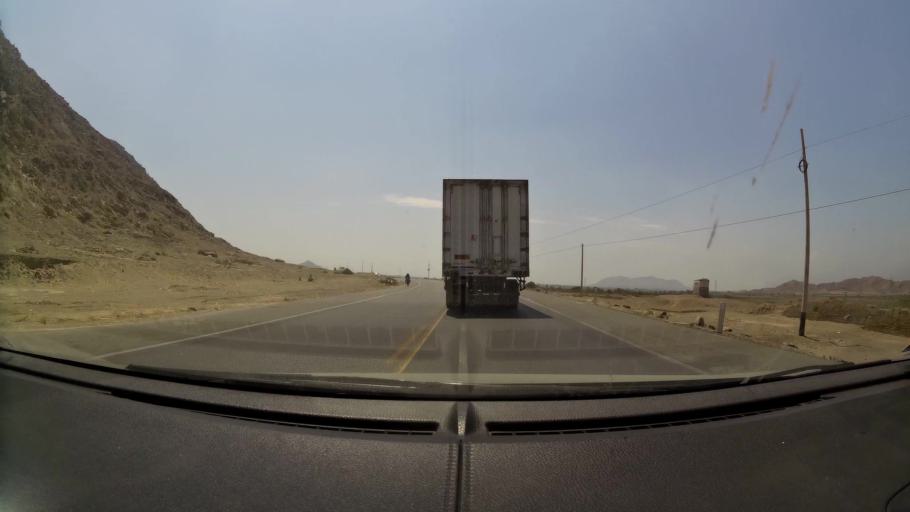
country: PE
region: La Libertad
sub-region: Provincia de Pacasmayo
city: Guadalupe
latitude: -7.2925
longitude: -79.4730
